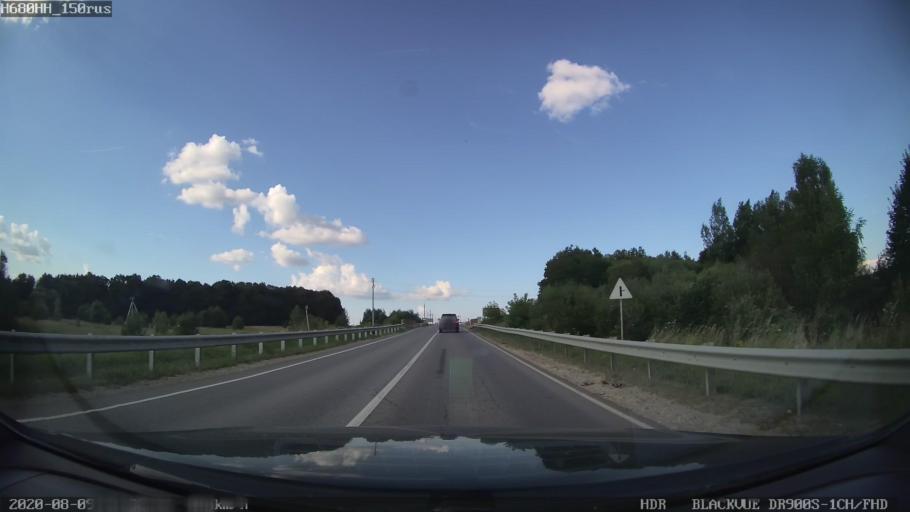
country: RU
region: Moskovskaya
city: Serpukhov
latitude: 54.8298
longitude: 37.4573
